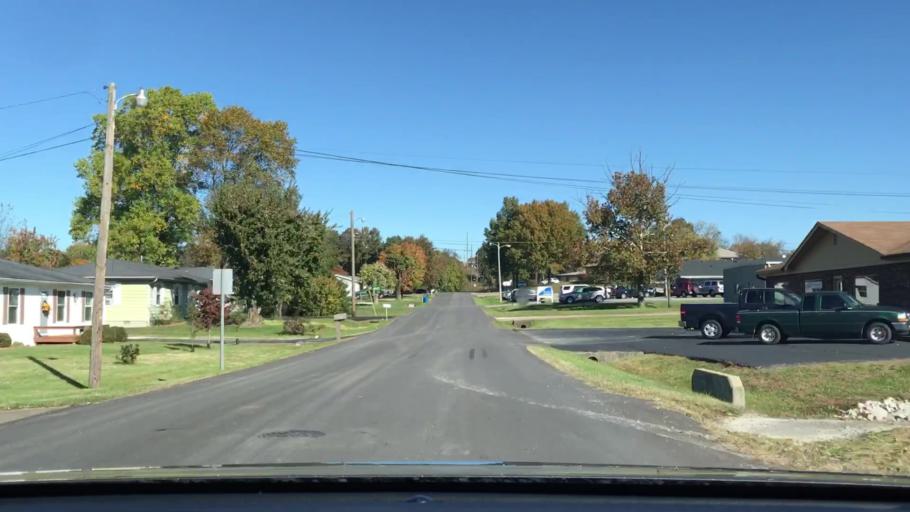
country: US
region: Kentucky
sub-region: Barren County
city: Glasgow
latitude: 36.9926
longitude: -85.9337
